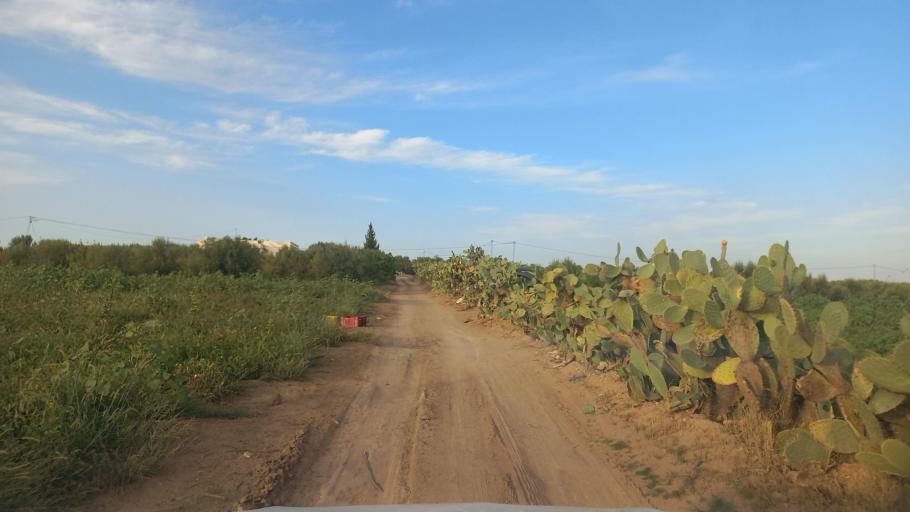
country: TN
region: Al Qasrayn
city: Kasserine
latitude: 35.2501
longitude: 9.0380
